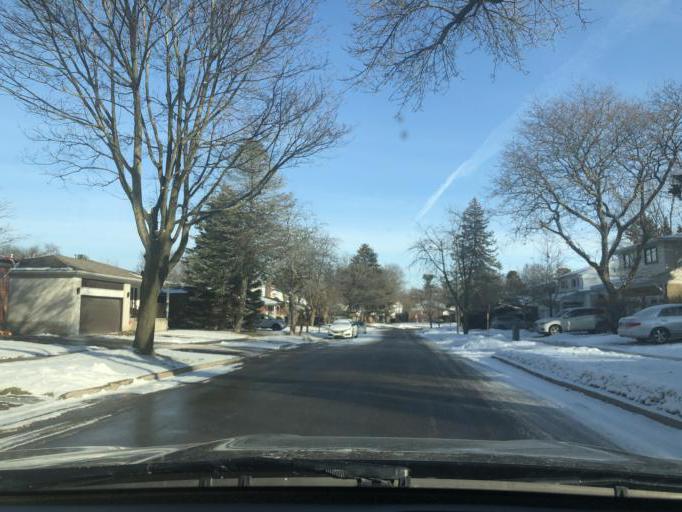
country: CA
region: Ontario
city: Scarborough
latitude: 43.7736
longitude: -79.1496
